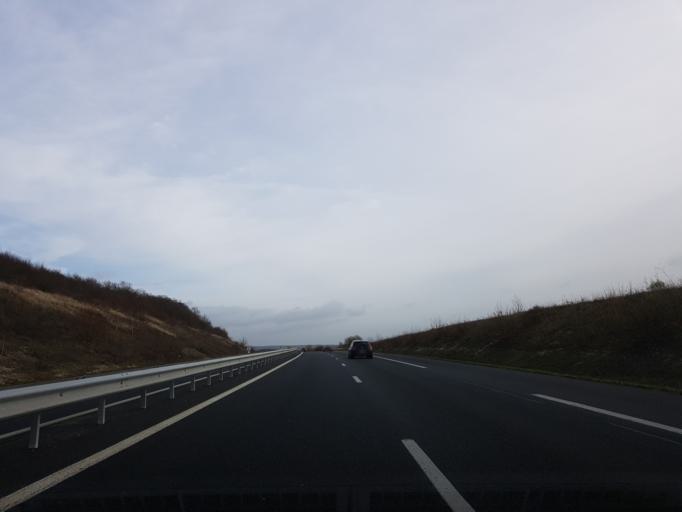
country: FR
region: Bourgogne
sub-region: Departement de l'Yonne
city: Thorigny-sur-Oreuse
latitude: 48.2410
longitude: 3.4811
